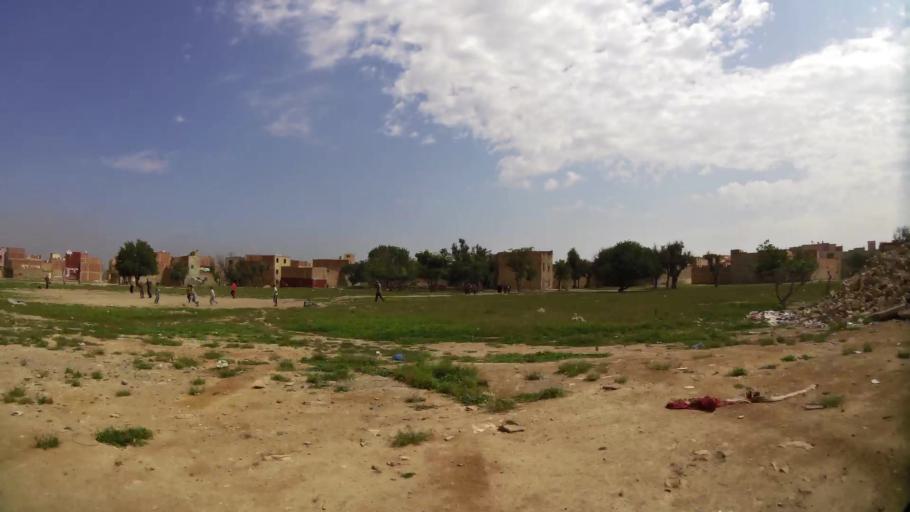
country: MA
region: Oriental
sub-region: Oujda-Angad
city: Oujda
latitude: 34.6809
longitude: -1.8953
